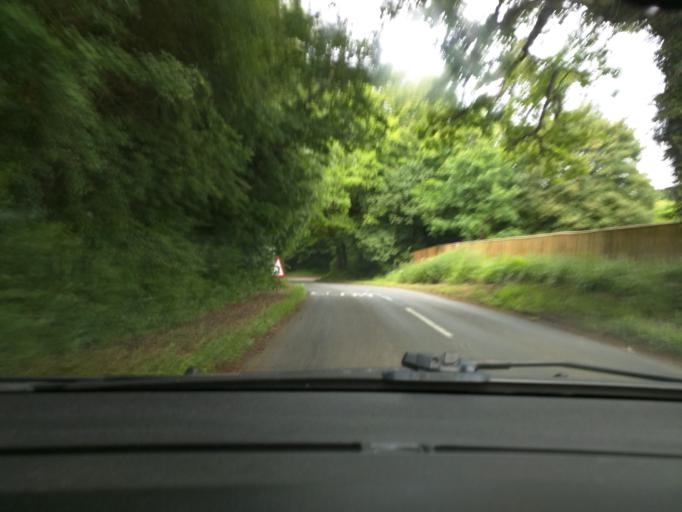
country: GB
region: England
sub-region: Suffolk
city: Saxmundham
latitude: 52.2280
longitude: 1.4497
